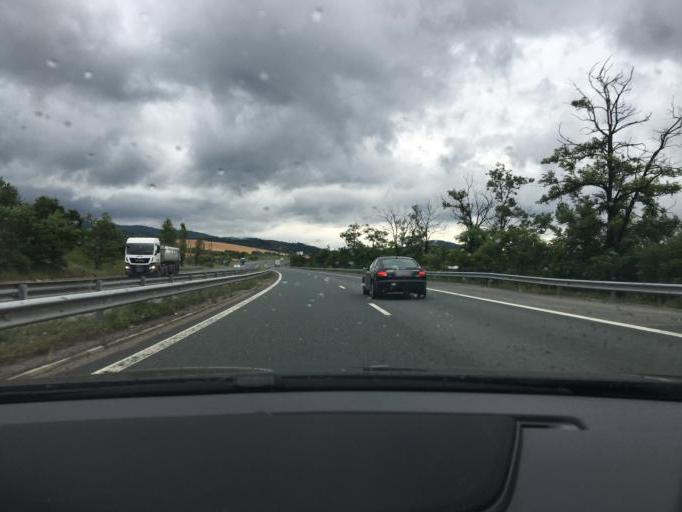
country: BG
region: Pernik
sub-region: Obshtina Pernik
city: Pernik
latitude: 42.5552
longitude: 23.1197
